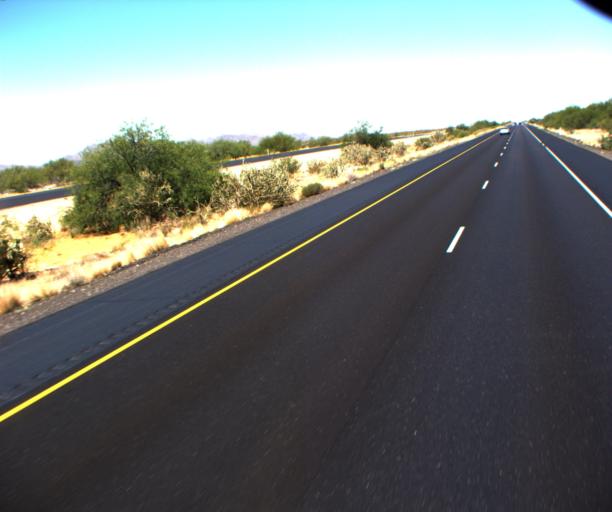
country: US
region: Arizona
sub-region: Yavapai County
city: Congress
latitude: 34.0668
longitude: -112.8691
